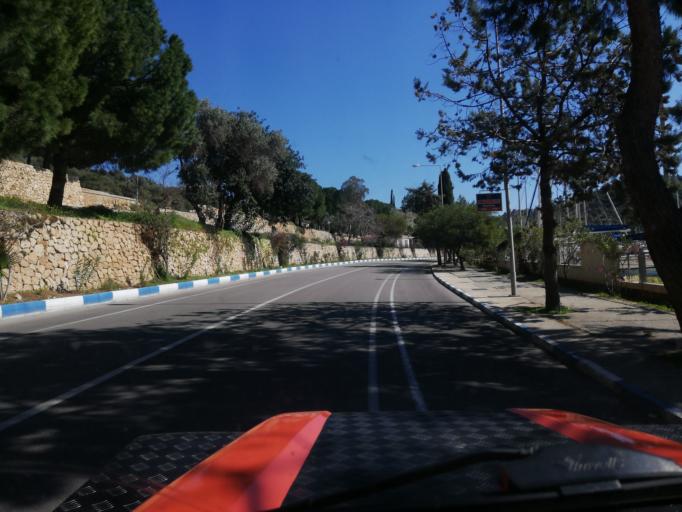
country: TR
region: Antalya
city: Kas
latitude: 36.2050
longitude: 29.6329
